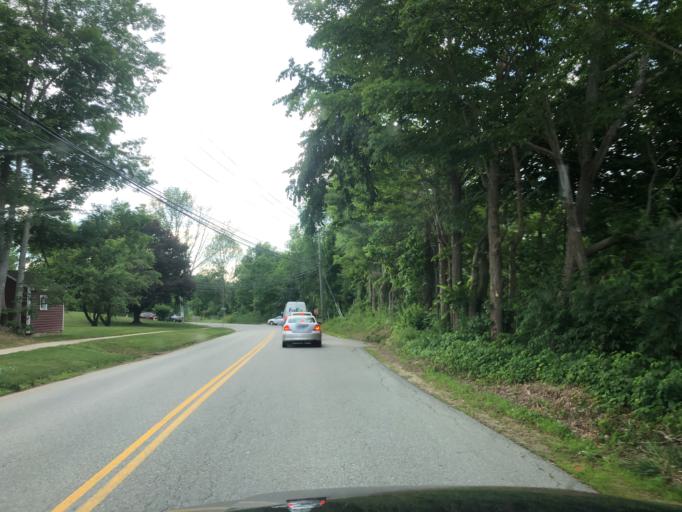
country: US
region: Connecticut
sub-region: New London County
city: Colchester
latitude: 41.5733
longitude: -72.3051
